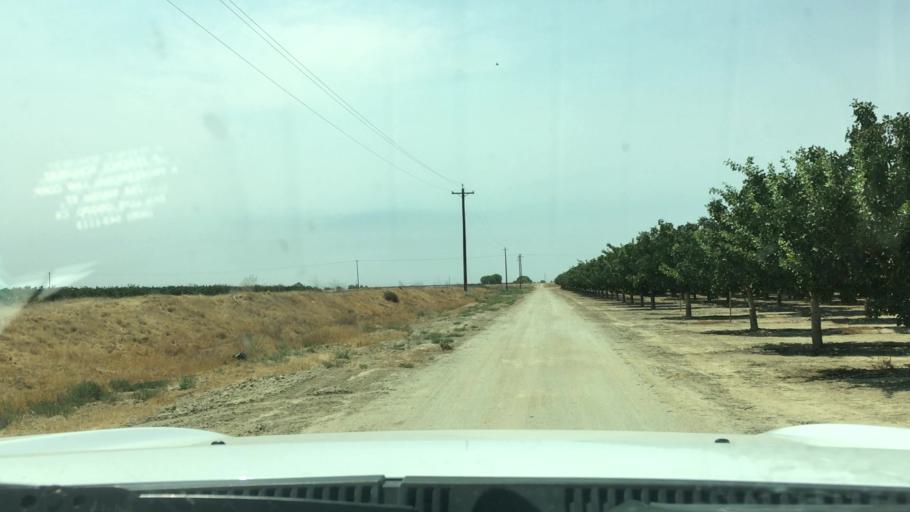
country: US
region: California
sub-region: Kern County
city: Wasco
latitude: 35.6813
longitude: -119.4335
